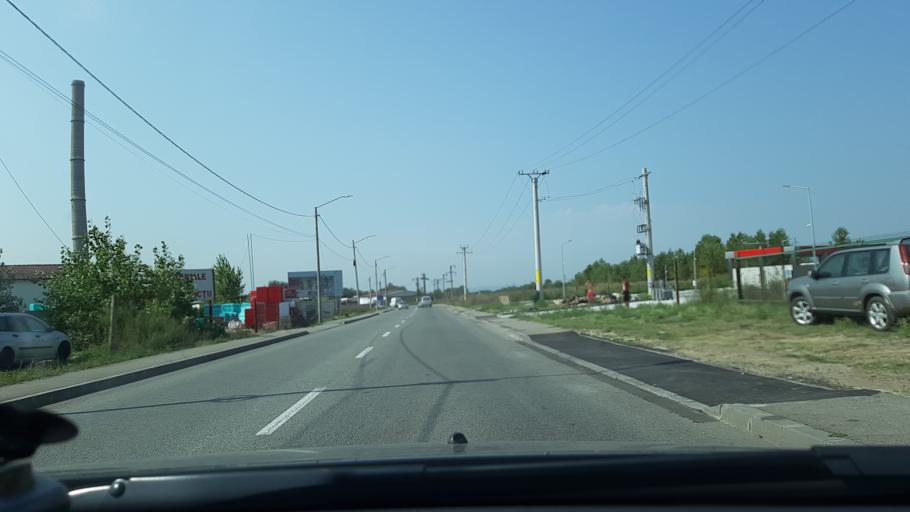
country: RO
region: Gorj
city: Targu Jiu
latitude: 45.0201
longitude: 23.2620
